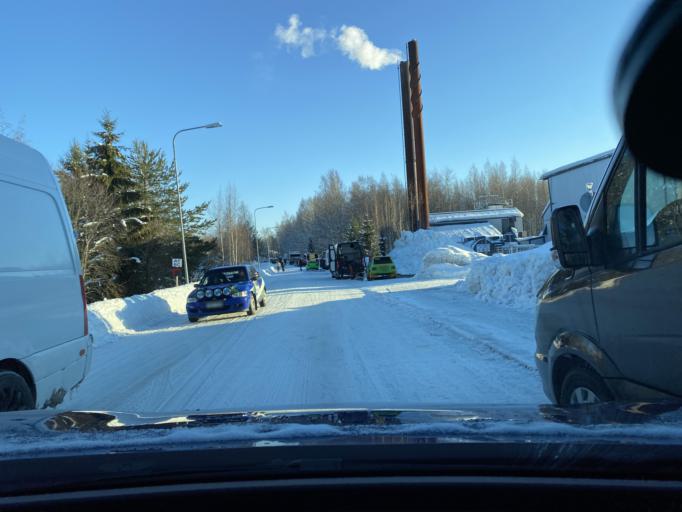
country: FI
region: Southern Savonia
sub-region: Mikkeli
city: Kangasniemi
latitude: 61.9865
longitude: 26.6376
